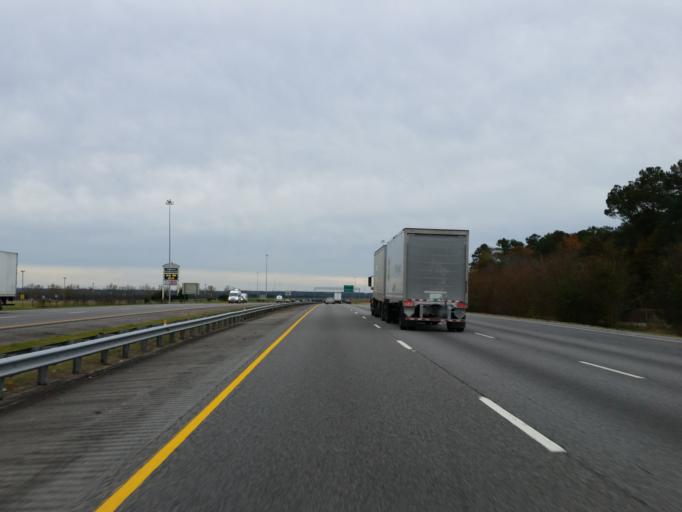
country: US
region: Georgia
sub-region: Houston County
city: Perry
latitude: 32.4432
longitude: -83.7552
